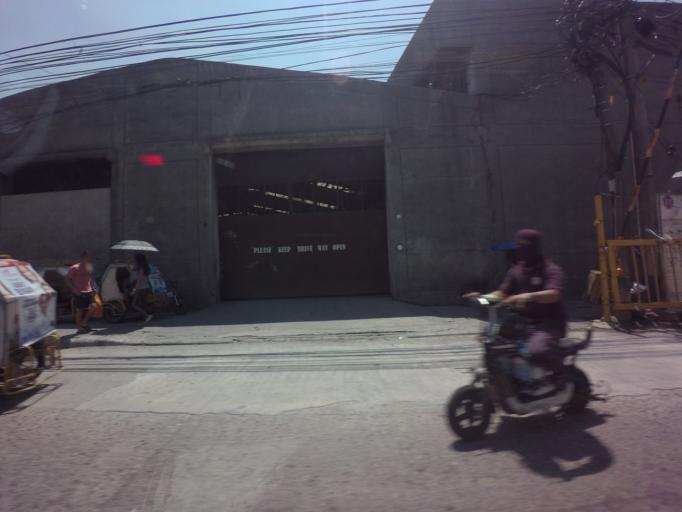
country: PH
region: Metro Manila
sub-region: Makati City
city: Makati City
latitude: 14.5572
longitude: 121.0056
